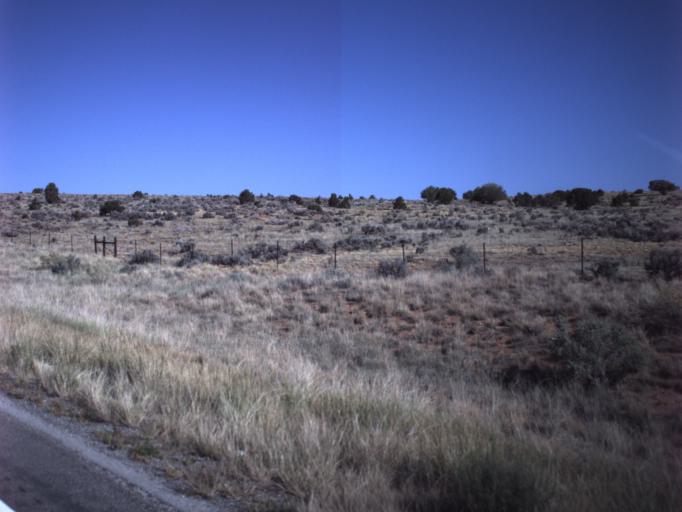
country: US
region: Utah
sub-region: Grand County
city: Moab
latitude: 38.3167
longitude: -109.4148
